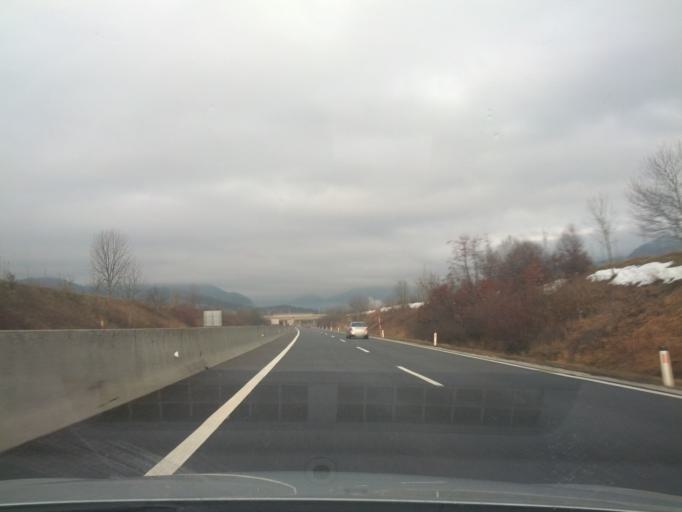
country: SI
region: Radovljica
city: Lesce
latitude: 46.3816
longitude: 14.1480
